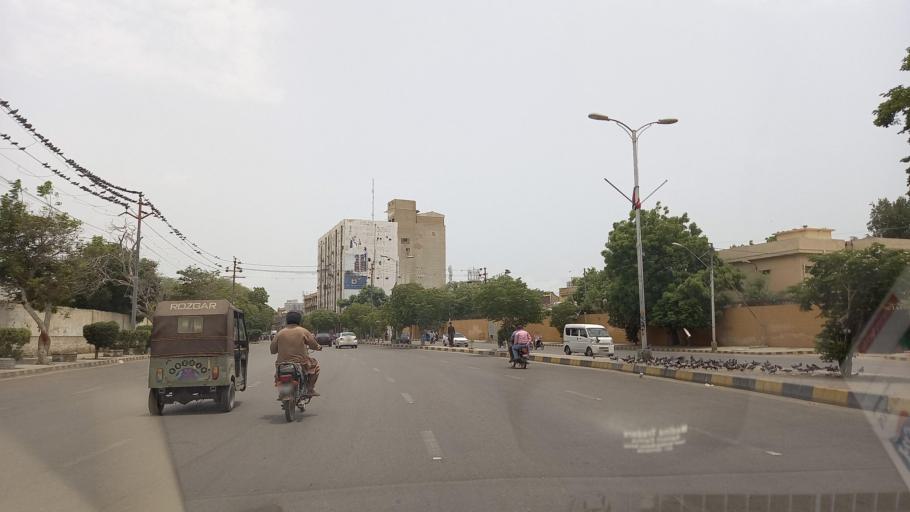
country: PK
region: Sindh
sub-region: Karachi District
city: Karachi
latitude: 24.8534
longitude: 67.0289
